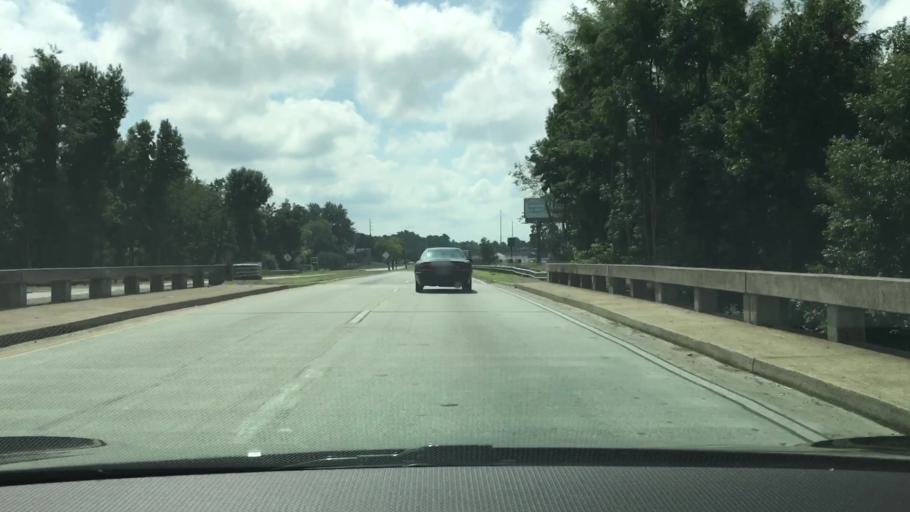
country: US
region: Georgia
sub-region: Hall County
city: Gainesville
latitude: 34.2923
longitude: -83.8147
